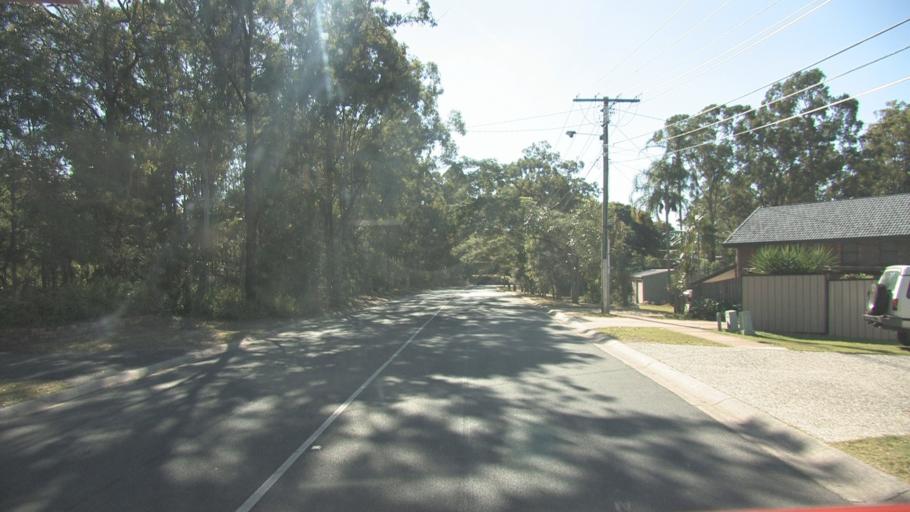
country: AU
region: Queensland
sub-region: Logan
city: Slacks Creek
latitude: -27.6687
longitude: 153.1680
